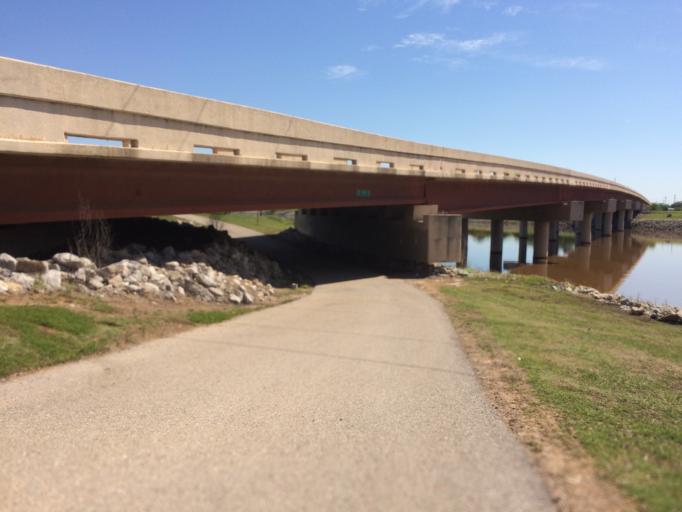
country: US
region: Oklahoma
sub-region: Oklahoma County
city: Oklahoma City
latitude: 35.4495
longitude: -97.5126
